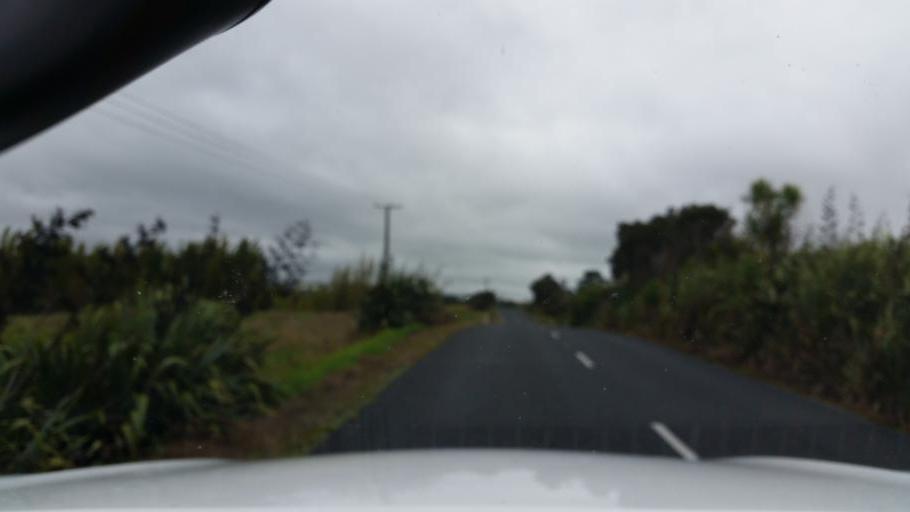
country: NZ
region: Northland
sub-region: Kaipara District
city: Dargaville
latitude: -36.1196
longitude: 173.9596
